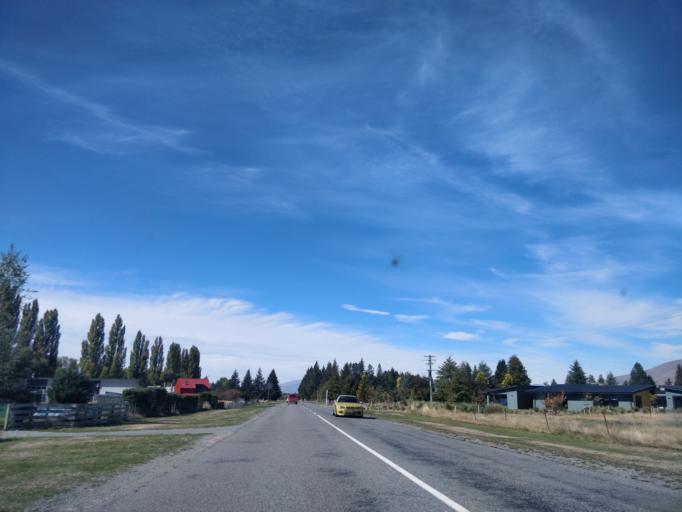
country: NZ
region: Otago
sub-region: Queenstown-Lakes District
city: Wanaka
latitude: -44.2429
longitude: 170.0882
